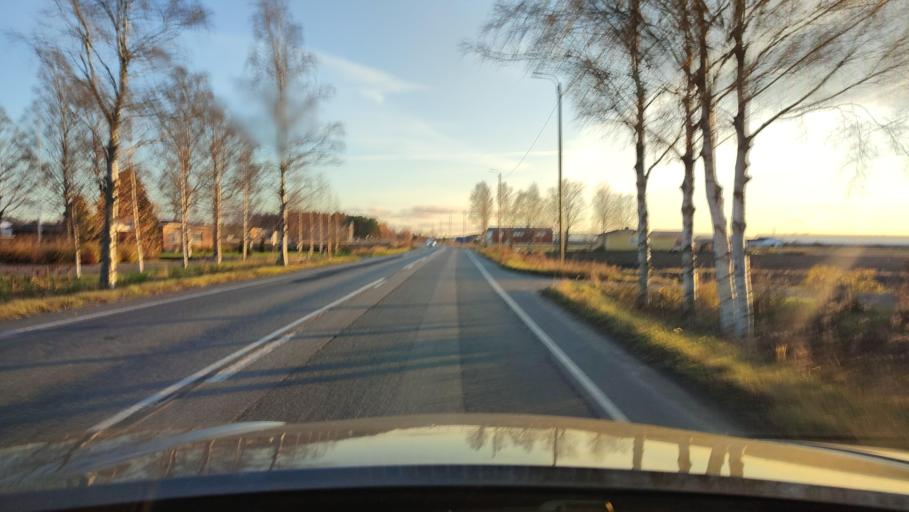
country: FI
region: Ostrobothnia
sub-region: Sydosterbotten
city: Naerpes
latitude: 62.4506
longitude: 21.3528
